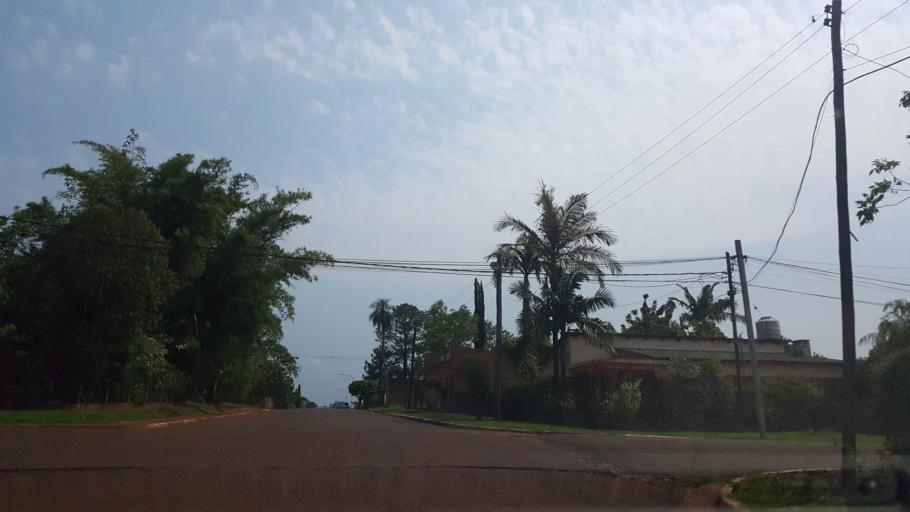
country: AR
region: Misiones
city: Gobernador Roca
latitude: -27.1899
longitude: -55.4698
